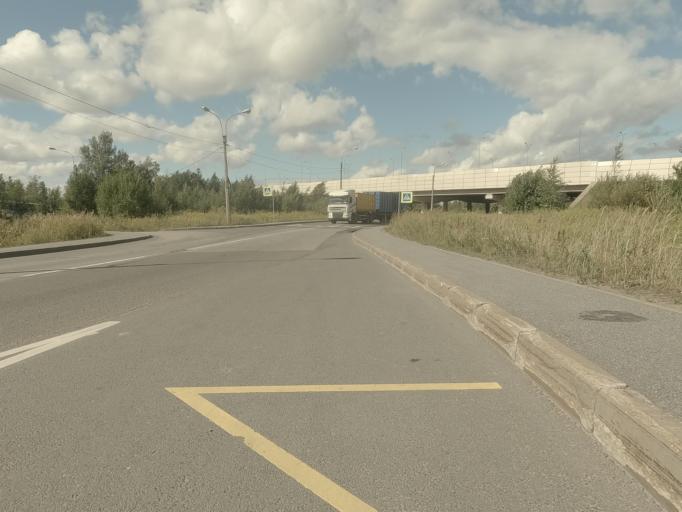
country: RU
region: St.-Petersburg
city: Krasnogvargeisky
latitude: 59.9749
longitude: 30.5354
